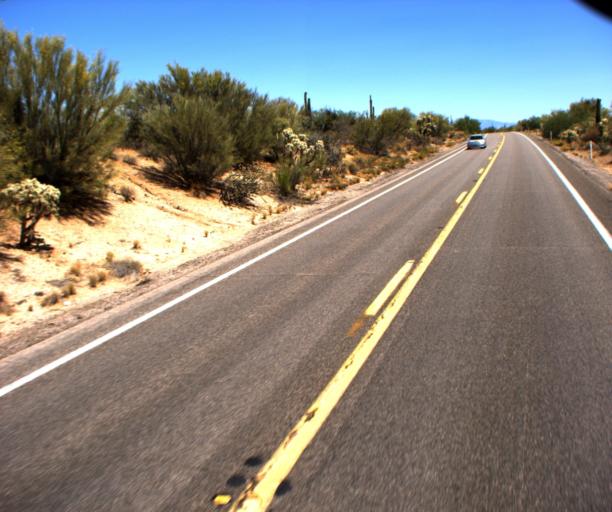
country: US
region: Arizona
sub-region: Pima County
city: Marana
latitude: 32.7709
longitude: -111.1587
